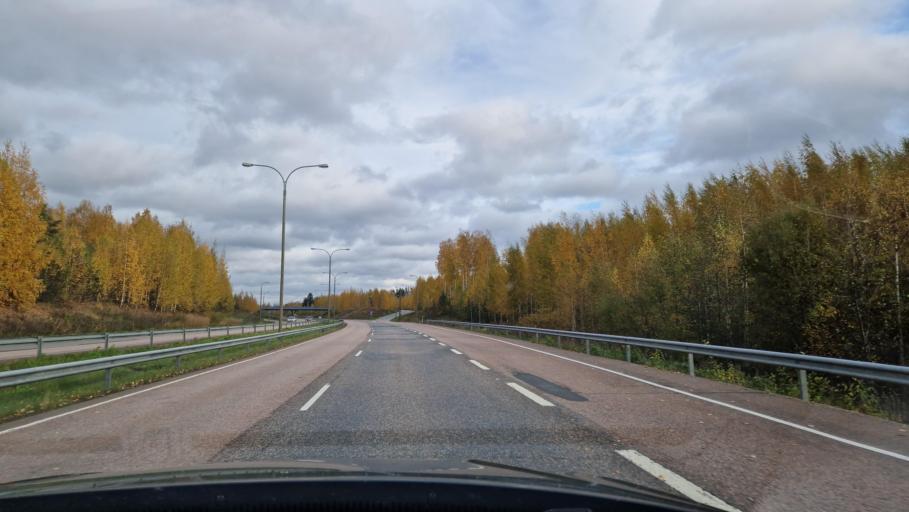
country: FI
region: Northern Savo
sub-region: Varkaus
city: Varkaus
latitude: 62.2836
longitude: 27.8713
